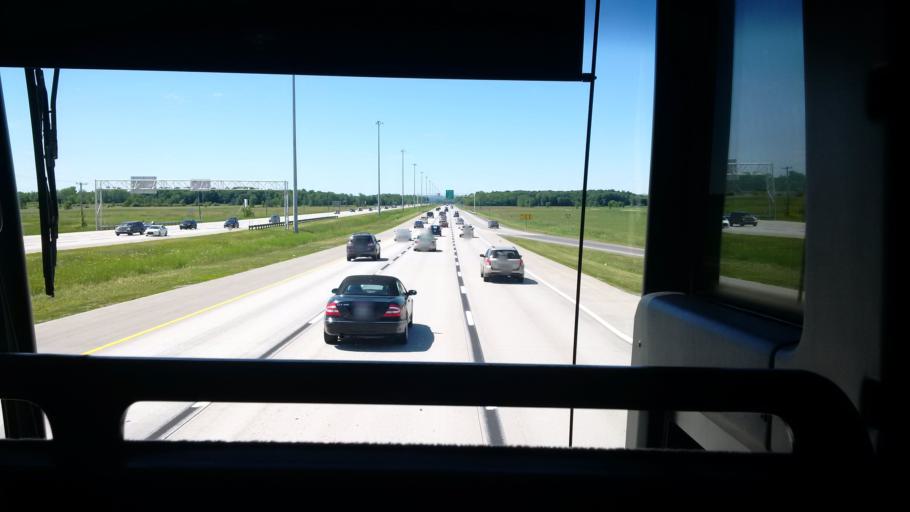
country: CA
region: Quebec
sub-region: Laurentides
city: Blainville
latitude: 45.6943
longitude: -73.9392
